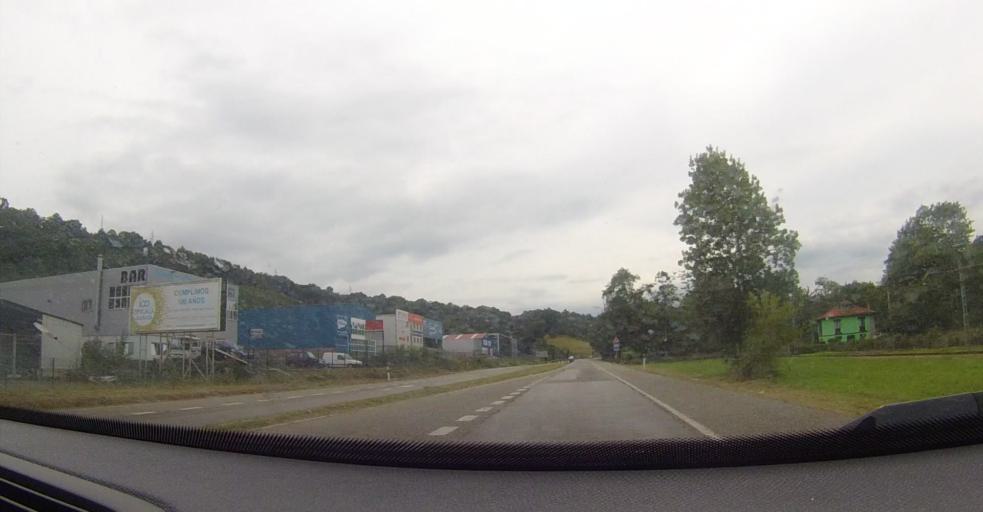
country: ES
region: Asturias
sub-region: Province of Asturias
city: Pilona
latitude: 43.3508
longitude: -5.3278
